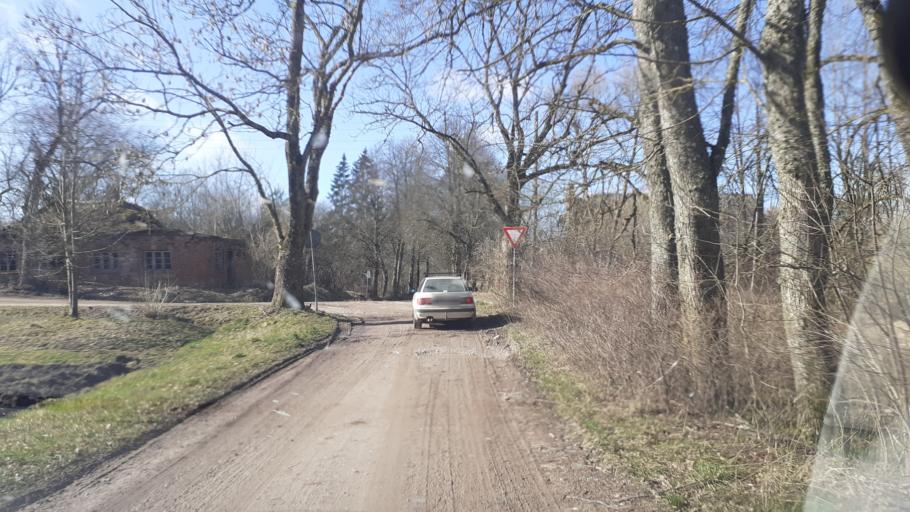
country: LV
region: Kuldigas Rajons
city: Kuldiga
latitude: 56.9341
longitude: 22.1569
